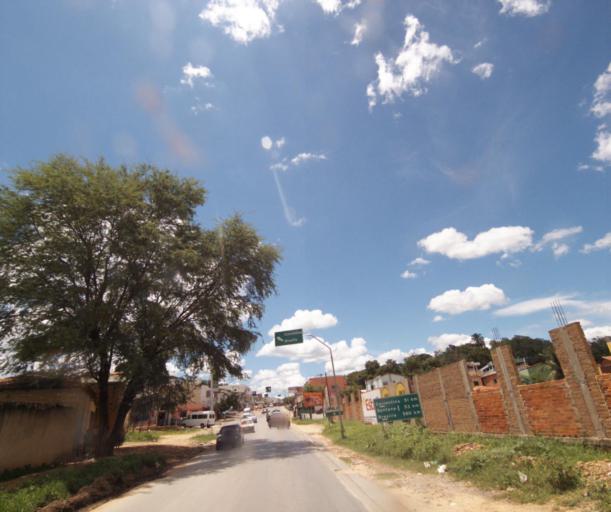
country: BR
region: Bahia
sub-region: Sao Felix Do Coribe
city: Santa Maria da Vitoria
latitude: -13.3992
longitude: -44.2024
